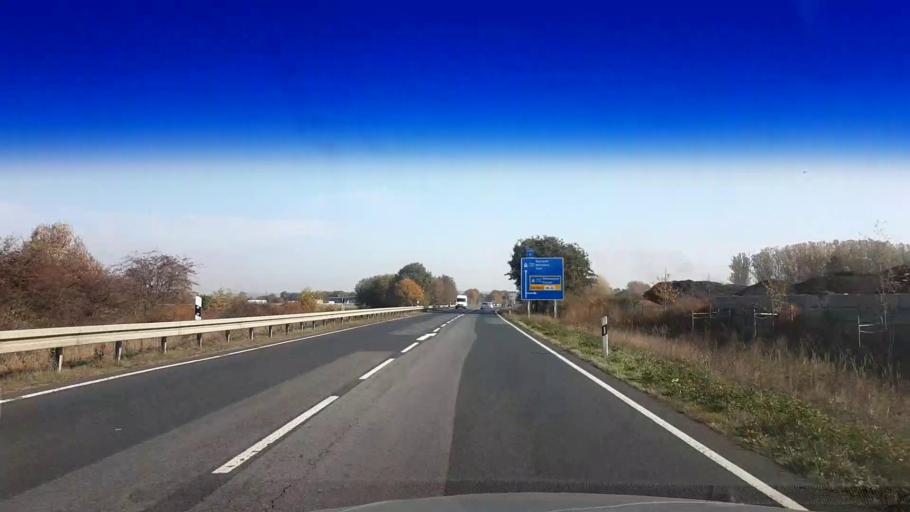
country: DE
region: Bavaria
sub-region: Upper Franconia
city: Bischberg
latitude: 49.9131
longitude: 10.8544
